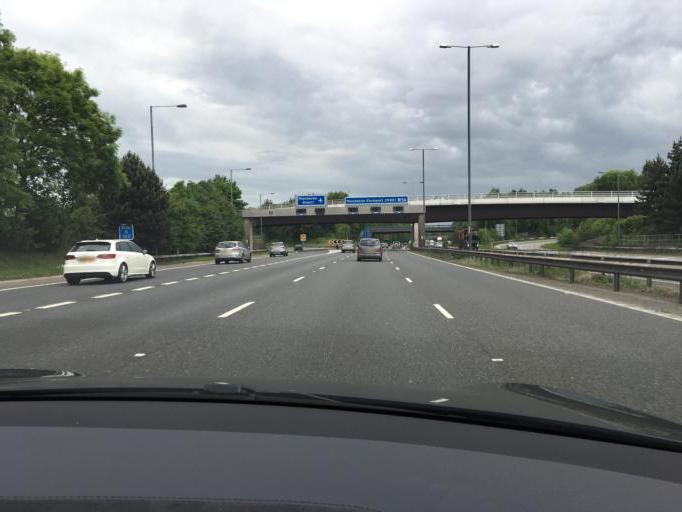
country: GB
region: England
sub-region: Manchester
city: Ringway
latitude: 53.3717
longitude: -2.2910
